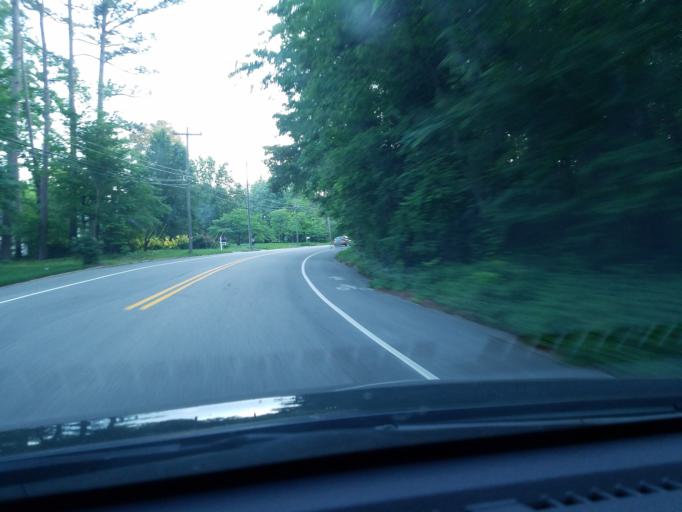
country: US
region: North Carolina
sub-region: Durham County
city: Durham
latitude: 35.9721
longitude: -78.9258
